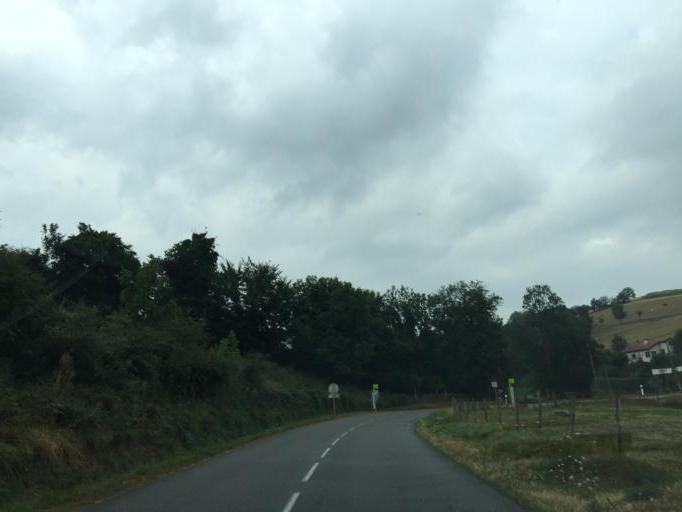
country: FR
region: Rhone-Alpes
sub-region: Departement de la Loire
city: Saint-Christo-en-Jarez
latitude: 45.5349
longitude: 4.4767
